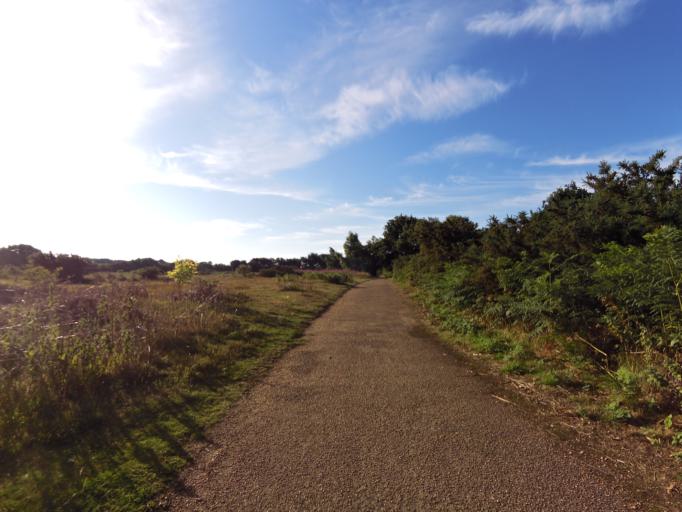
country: GB
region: England
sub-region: Suffolk
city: Kesgrave
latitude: 52.0680
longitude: 1.2735
